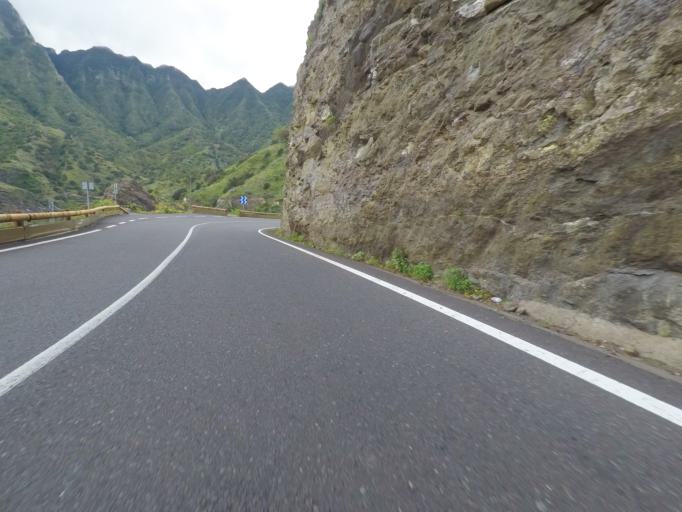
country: ES
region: Canary Islands
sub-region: Provincia de Santa Cruz de Tenerife
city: Hermigua
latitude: 28.1456
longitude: -17.1991
